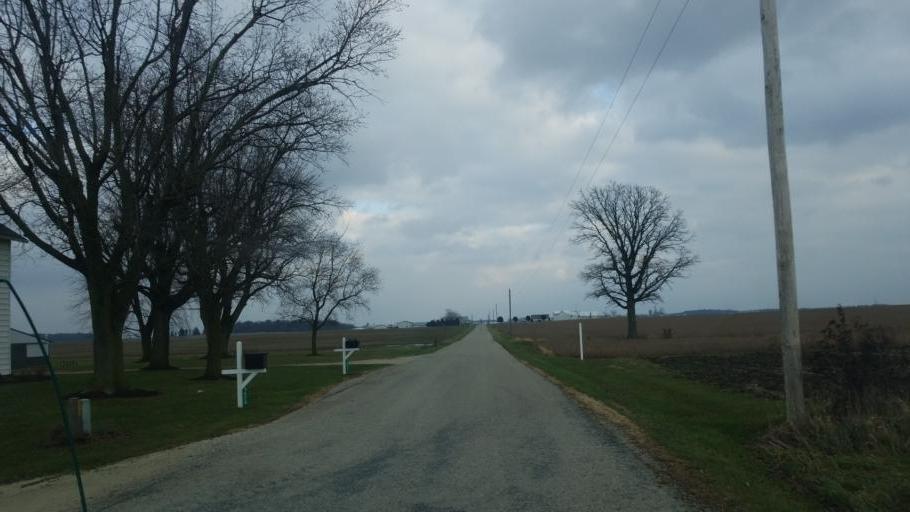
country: US
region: Ohio
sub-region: Mercer County
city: Fort Recovery
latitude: 40.5136
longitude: -84.8153
